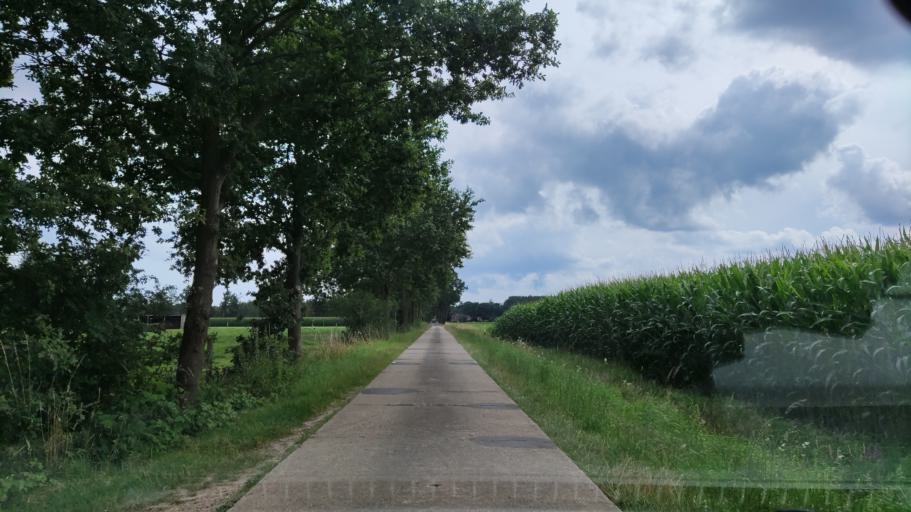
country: DE
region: Lower Saxony
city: Damnatz
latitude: 53.1022
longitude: 11.1446
